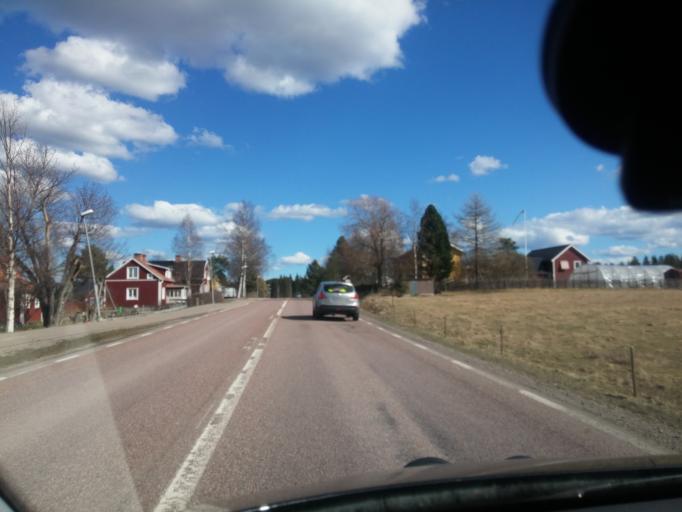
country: SE
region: Gaevleborg
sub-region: Ljusdals Kommun
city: Farila
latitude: 61.8009
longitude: 15.8824
